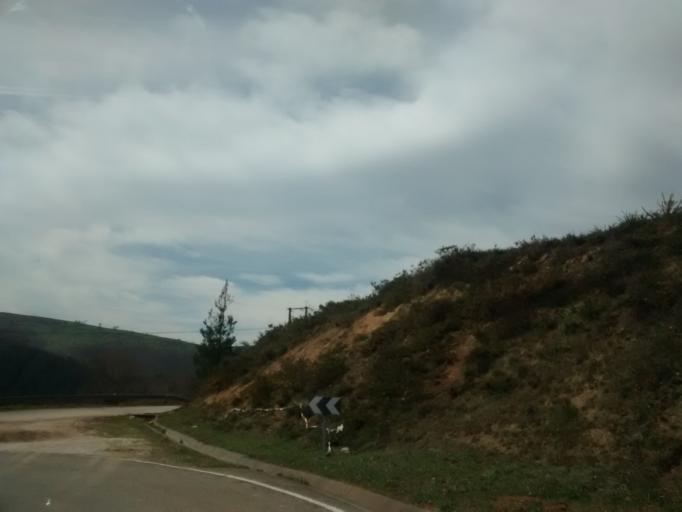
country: ES
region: Cantabria
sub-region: Provincia de Cantabria
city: Vega de Pas
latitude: 43.1637
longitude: -3.7941
